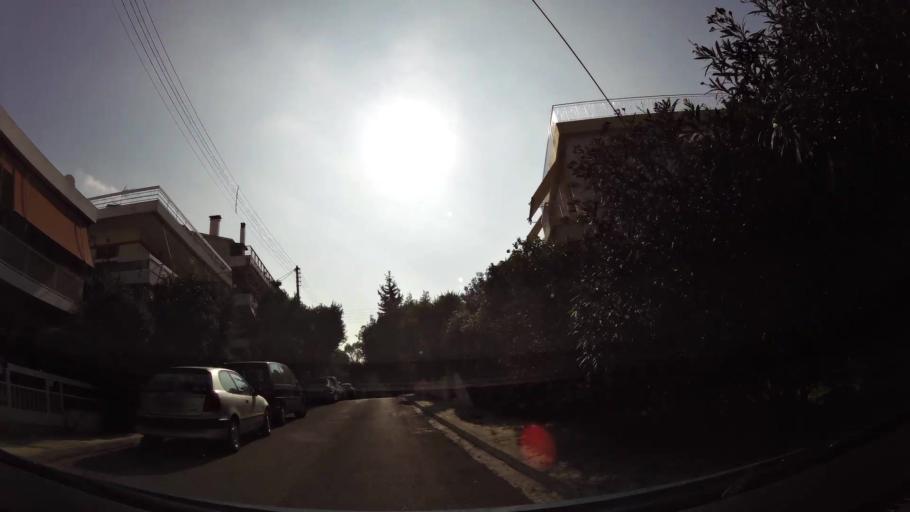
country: GR
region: Attica
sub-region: Nomos Attikis
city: Zografos
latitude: 37.9767
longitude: 23.7923
